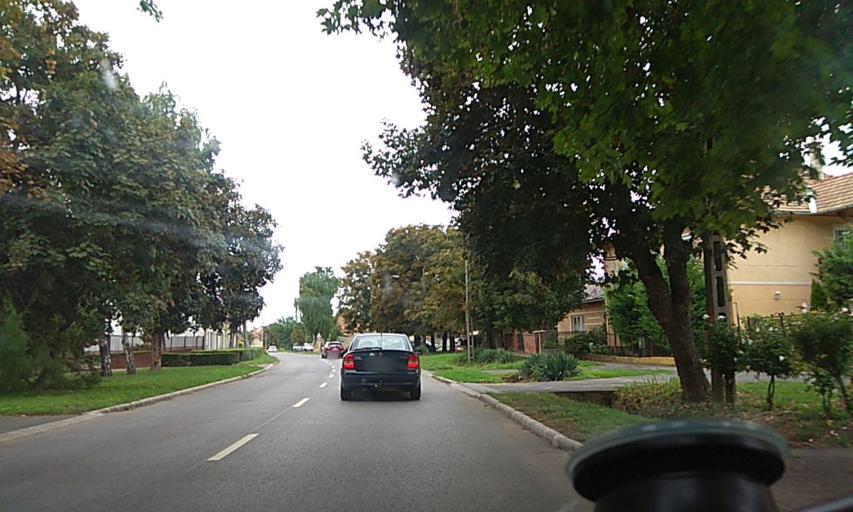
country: HU
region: Borsod-Abauj-Zemplen
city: Tarcal
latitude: 48.1306
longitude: 21.3441
